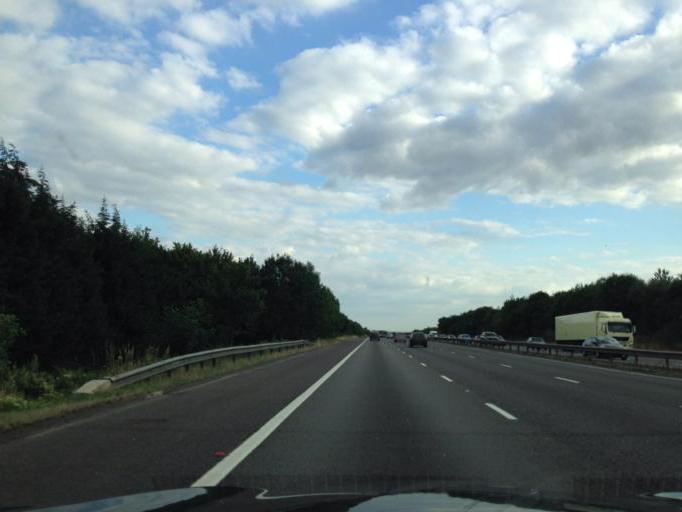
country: GB
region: England
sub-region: Oxfordshire
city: Bicester
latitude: 51.9005
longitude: -1.2058
